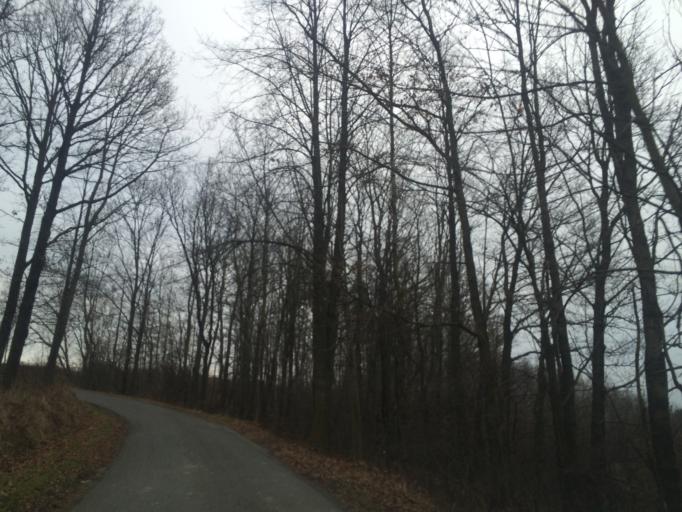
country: PL
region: Lower Silesian Voivodeship
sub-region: Powiat klodzki
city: Bystrzyca Klodzka
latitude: 50.2509
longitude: 16.6980
